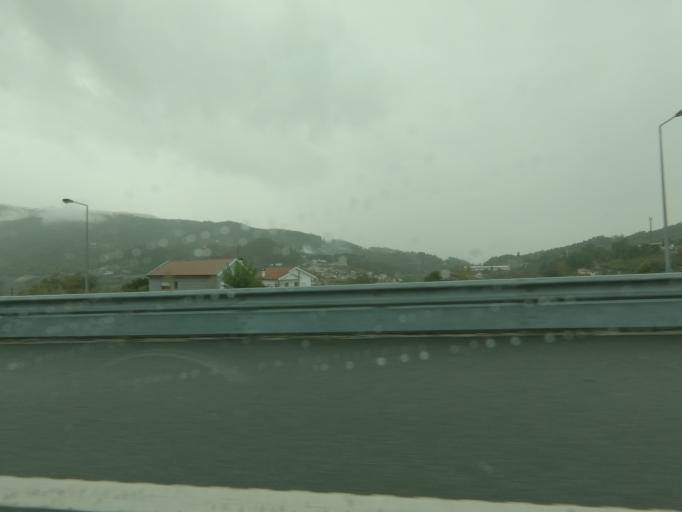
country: PT
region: Porto
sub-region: Amarante
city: Amarante
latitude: 41.2561
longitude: -8.0489
